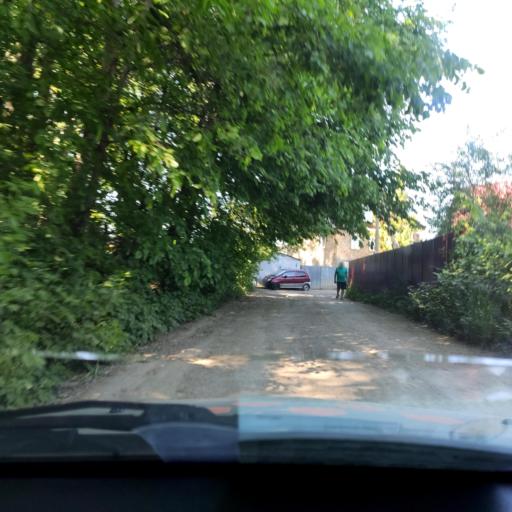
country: RU
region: Bashkortostan
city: Ufa
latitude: 54.7851
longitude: 56.1849
